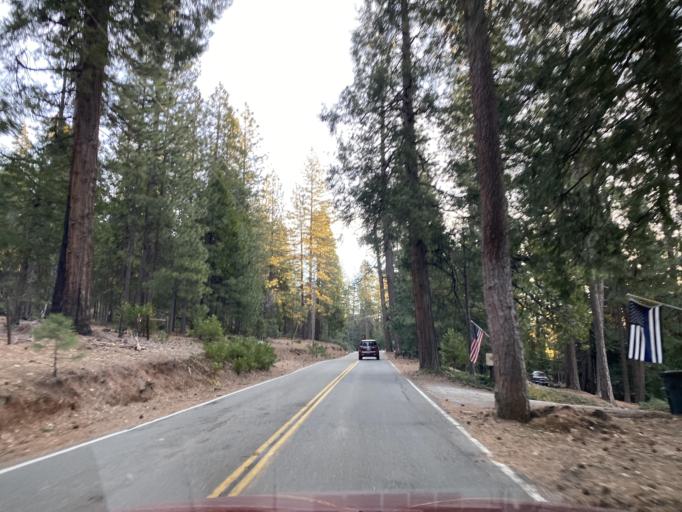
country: US
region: California
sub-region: Amador County
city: Pioneer
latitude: 38.5020
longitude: -120.5407
